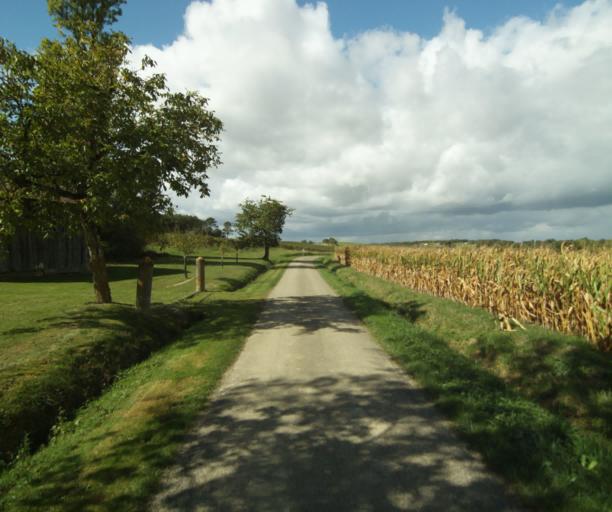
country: FR
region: Midi-Pyrenees
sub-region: Departement du Gers
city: Nogaro
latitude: 43.8453
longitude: -0.0276
